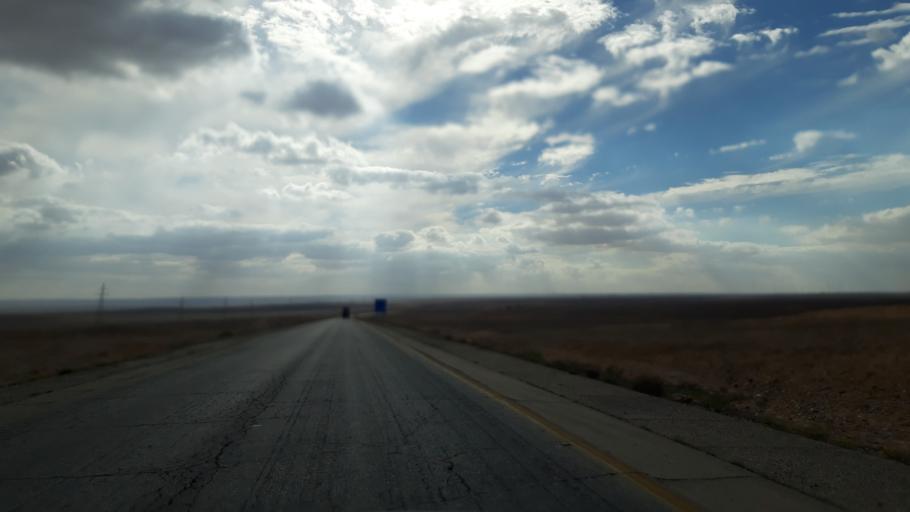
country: JO
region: Amman
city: Al Azraq ash Shamali
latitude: 31.7358
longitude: 36.5179
